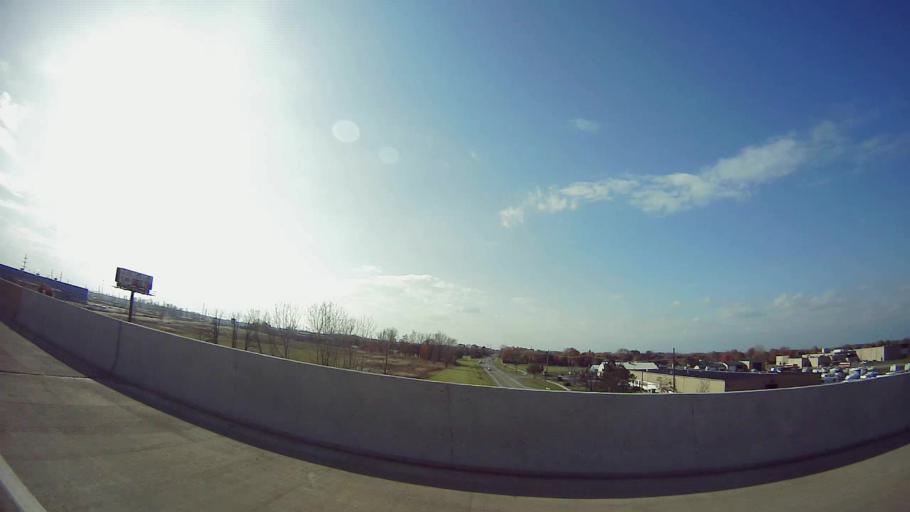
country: US
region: Michigan
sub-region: Wayne County
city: Woodhaven
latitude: 42.1243
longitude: -83.2415
